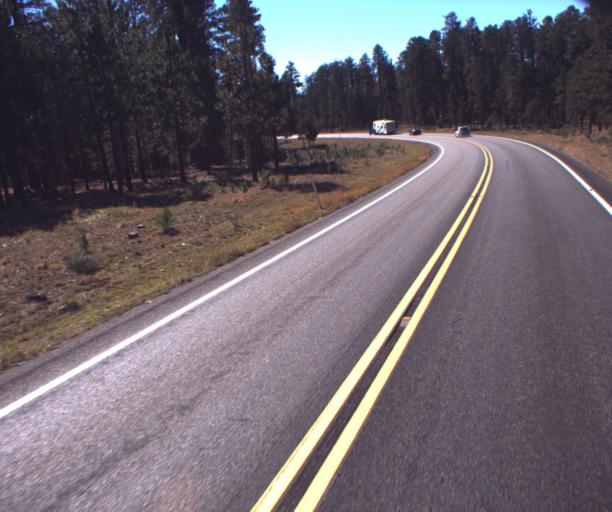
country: US
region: Arizona
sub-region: Coconino County
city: Fredonia
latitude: 36.6875
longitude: -112.2184
